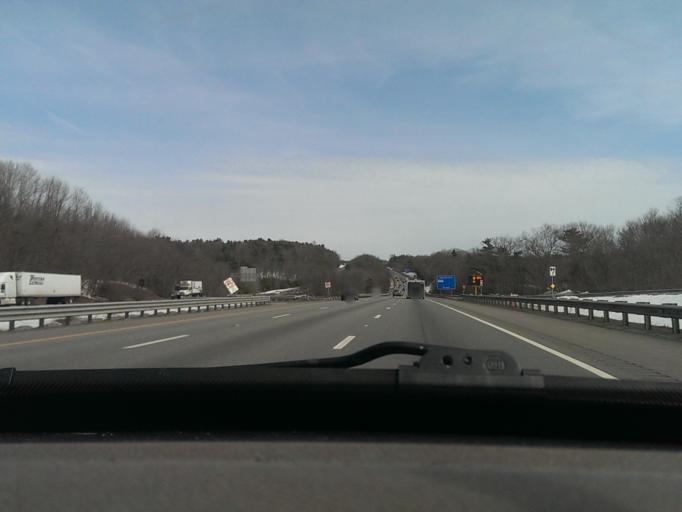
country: US
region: Massachusetts
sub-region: Worcester County
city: Sturbridge
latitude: 42.1352
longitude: -72.0416
